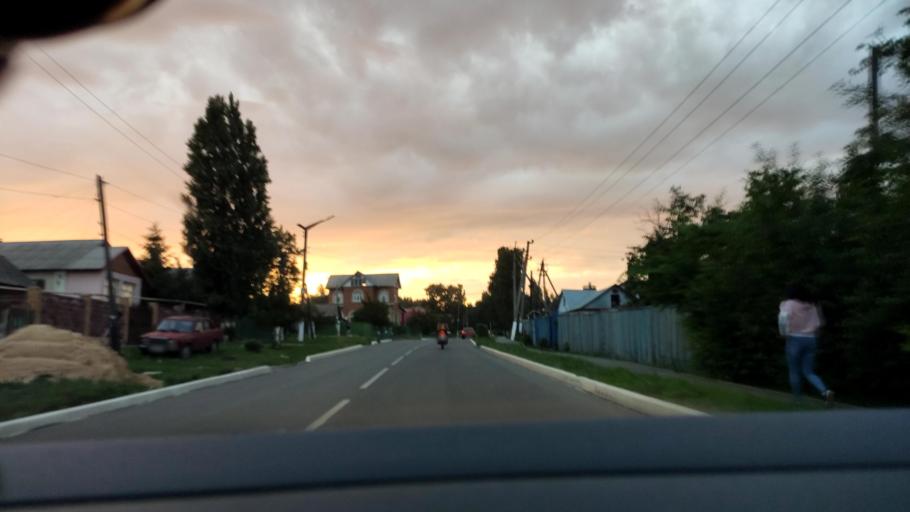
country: RU
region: Voronezj
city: Semiluki
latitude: 51.6885
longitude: 39.0243
